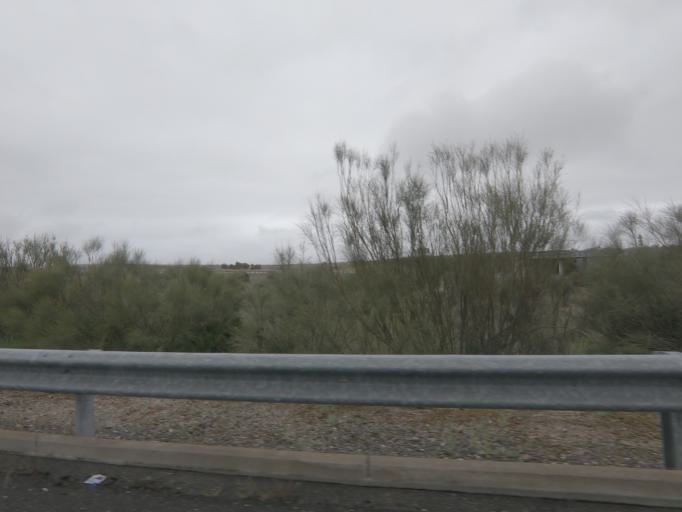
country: ES
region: Extremadura
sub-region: Provincia de Caceres
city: Casar de Caceres
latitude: 39.5368
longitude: -6.4092
